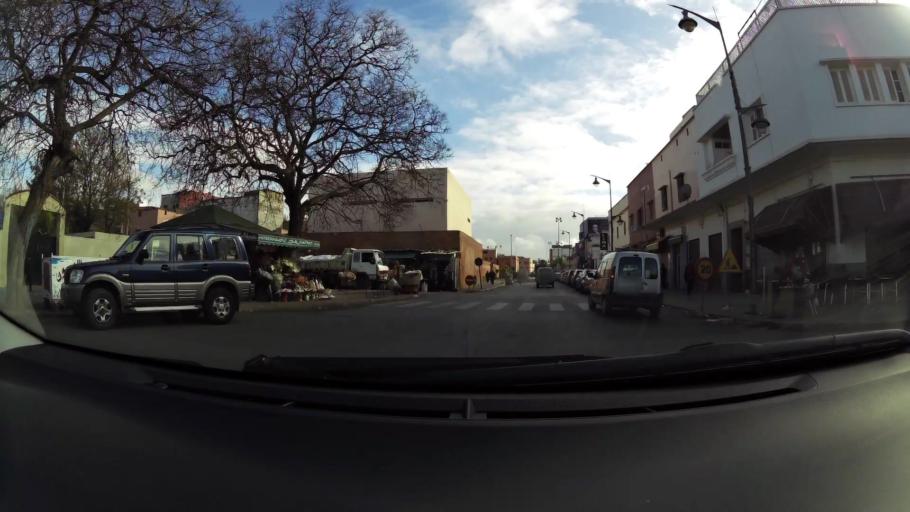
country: MA
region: Grand Casablanca
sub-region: Mohammedia
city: Mohammedia
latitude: 33.7004
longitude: -7.3879
